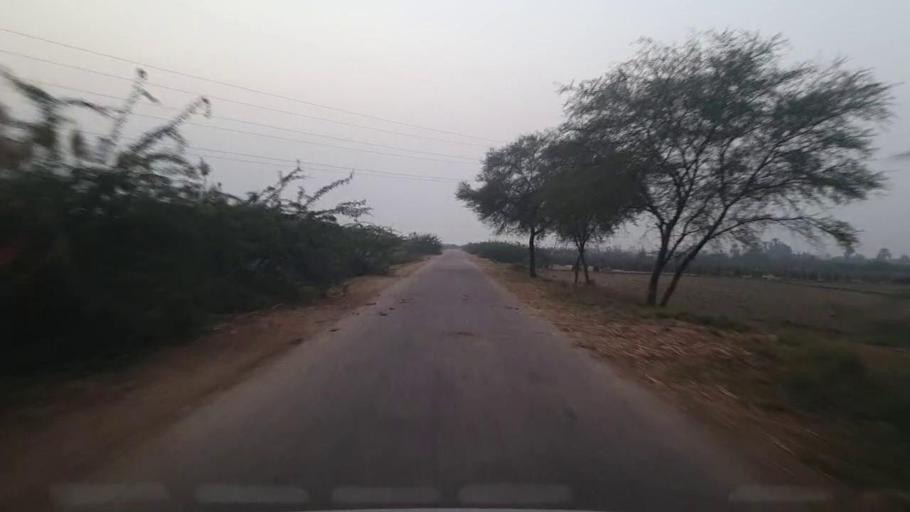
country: PK
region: Sindh
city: Gambat
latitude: 27.3406
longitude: 68.6109
